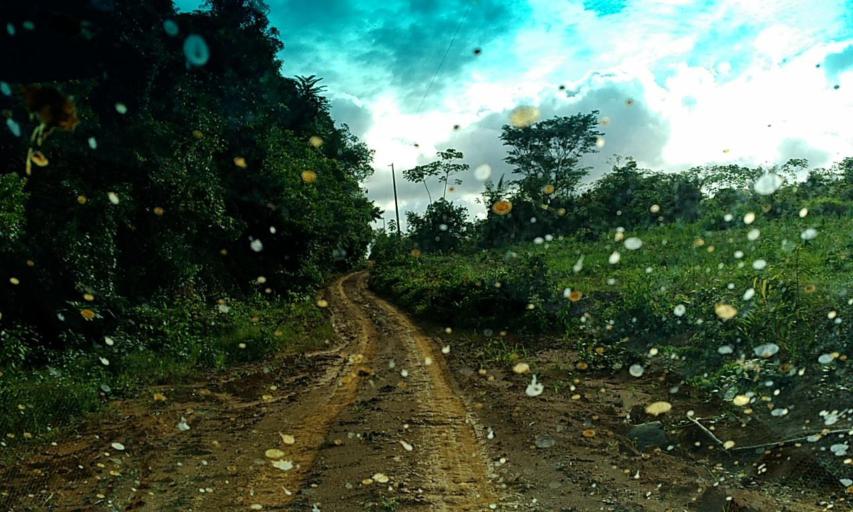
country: BR
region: Para
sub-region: Senador Jose Porfirio
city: Senador Jose Porfirio
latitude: -3.0078
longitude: -51.7453
